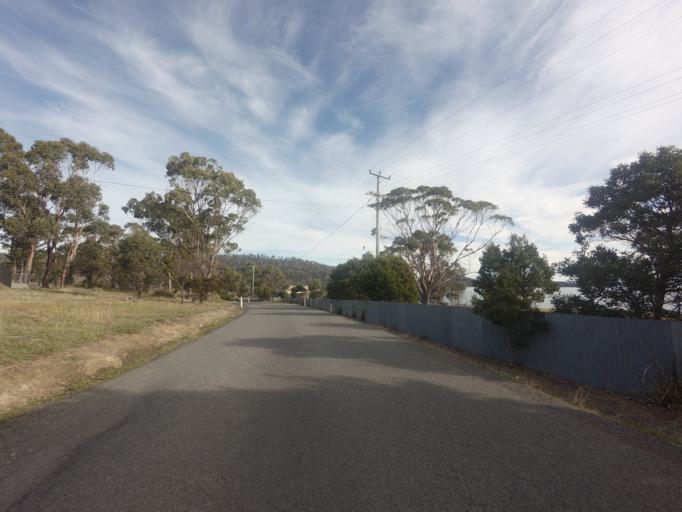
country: AU
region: Tasmania
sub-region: Sorell
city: Sorell
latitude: -42.9524
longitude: 147.8508
